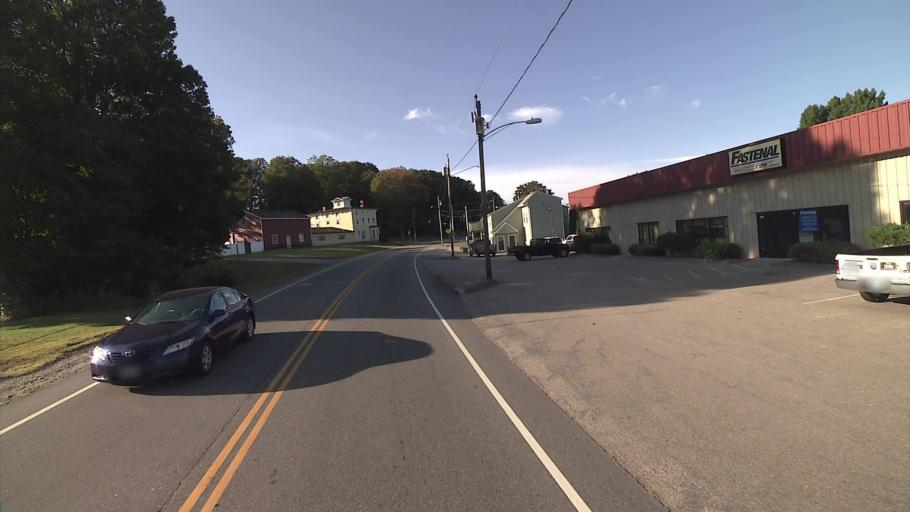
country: US
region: Connecticut
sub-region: New London County
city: Baltic
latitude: 41.5928
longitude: -72.1289
